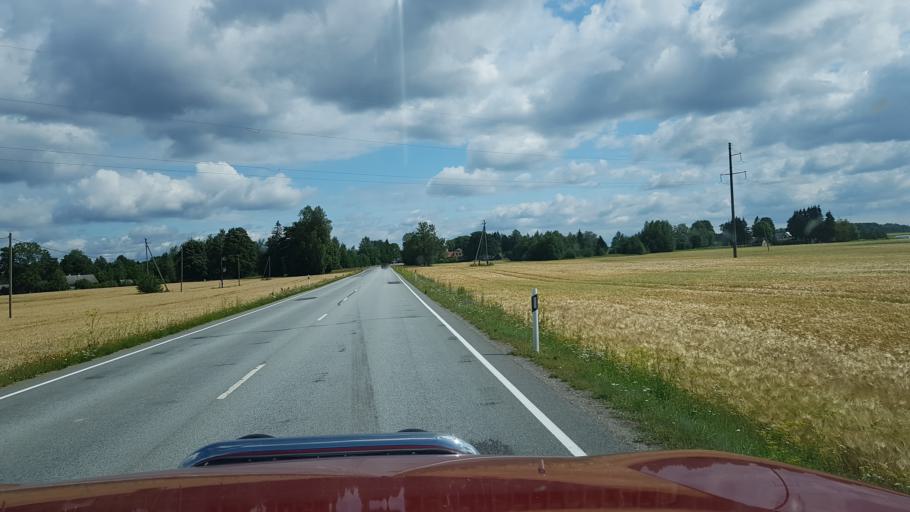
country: EE
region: Jogevamaa
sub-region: Jogeva linn
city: Jogeva
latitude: 58.8223
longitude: 26.5827
